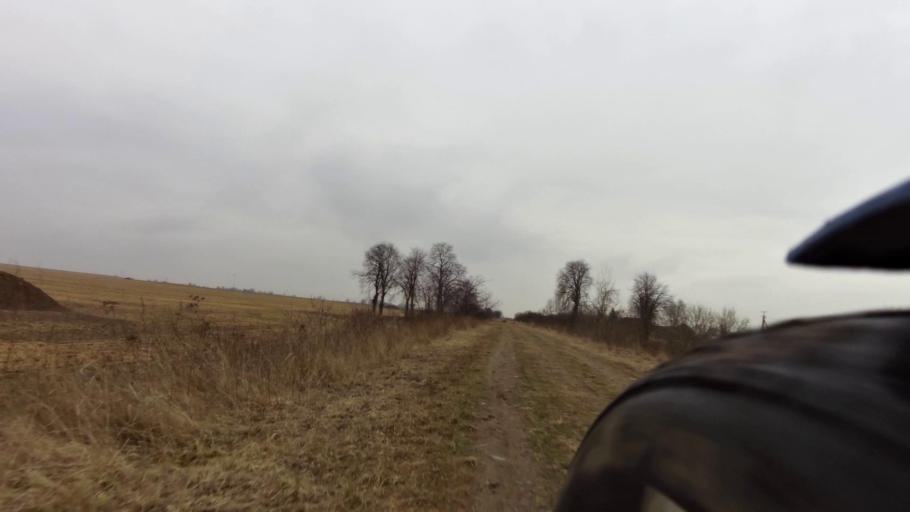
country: PL
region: West Pomeranian Voivodeship
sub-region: Powiat walecki
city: Walcz
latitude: 53.2439
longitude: 16.4717
